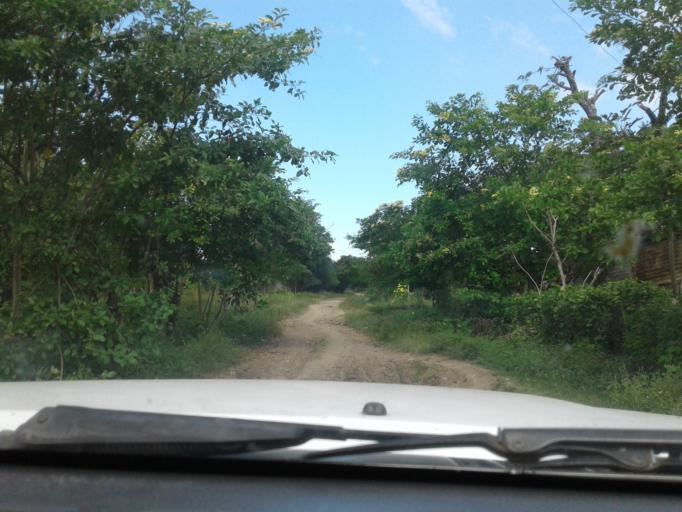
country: NI
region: Rivas
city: Belen
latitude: 11.6295
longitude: -85.9525
